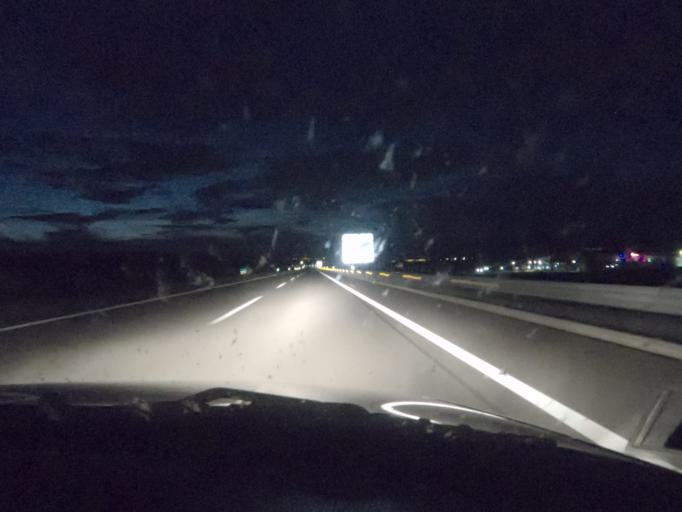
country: ES
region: Extremadura
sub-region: Provincia de Caceres
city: Casas de Don Gomez
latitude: 40.0202
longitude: -6.5932
